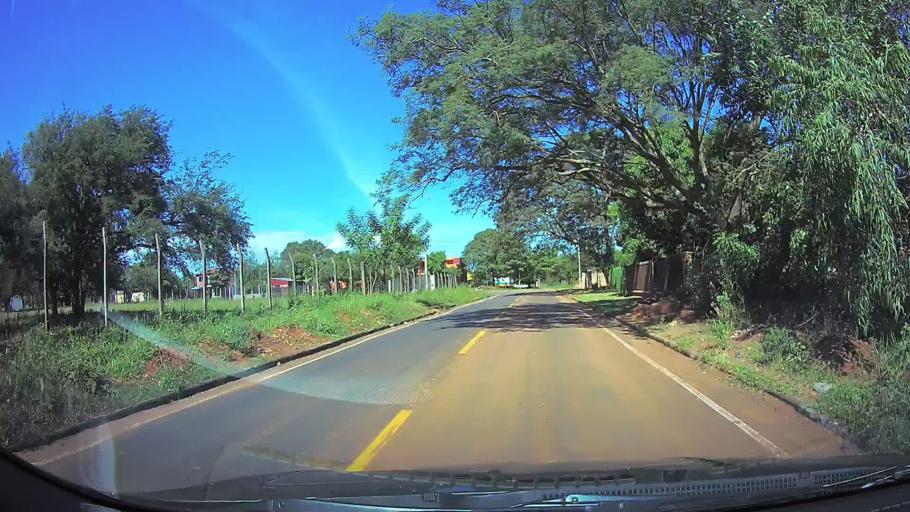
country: PY
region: Central
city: San Lorenzo
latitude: -25.2606
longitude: -57.4659
